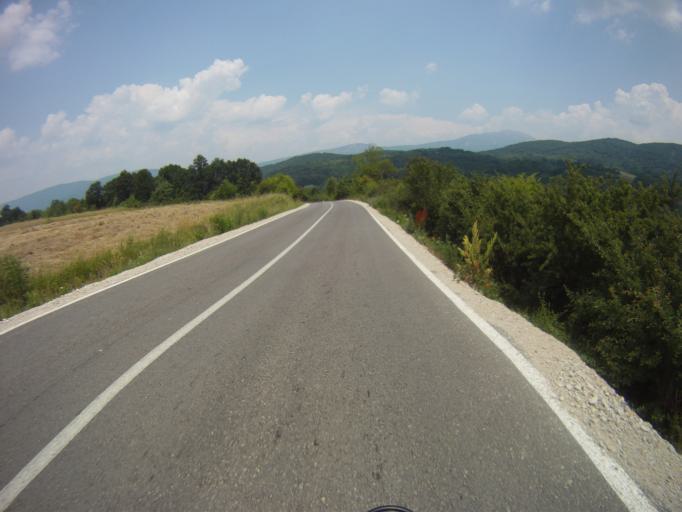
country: RS
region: Central Serbia
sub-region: Nisavski Okrug
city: Gadzin Han
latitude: 43.2085
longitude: 22.0197
